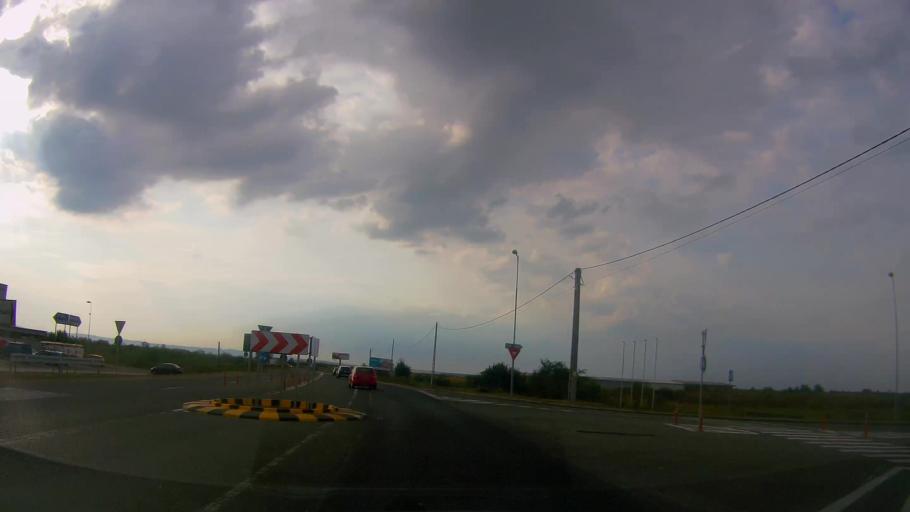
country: RO
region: Satu Mare
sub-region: Oras Ardud
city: Madaras
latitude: 47.7295
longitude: 22.8824
